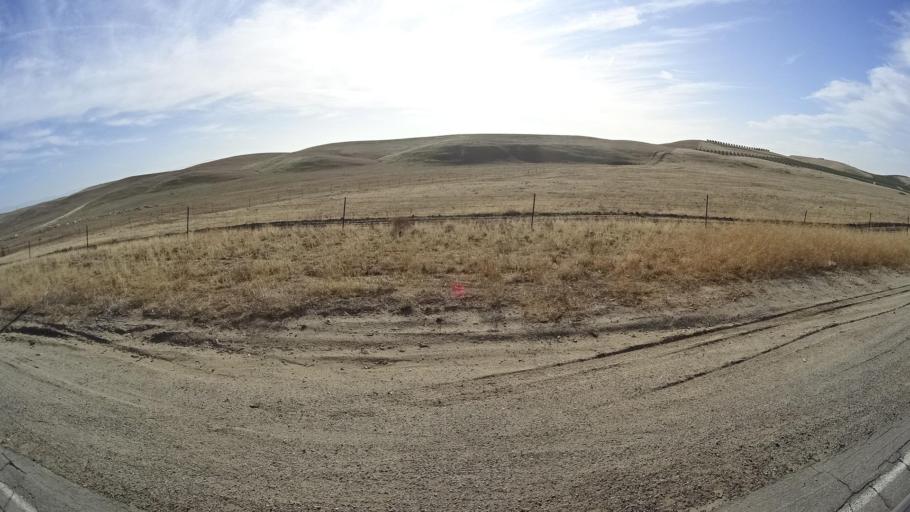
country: US
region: California
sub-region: Kern County
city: McFarland
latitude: 35.6076
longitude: -119.0640
